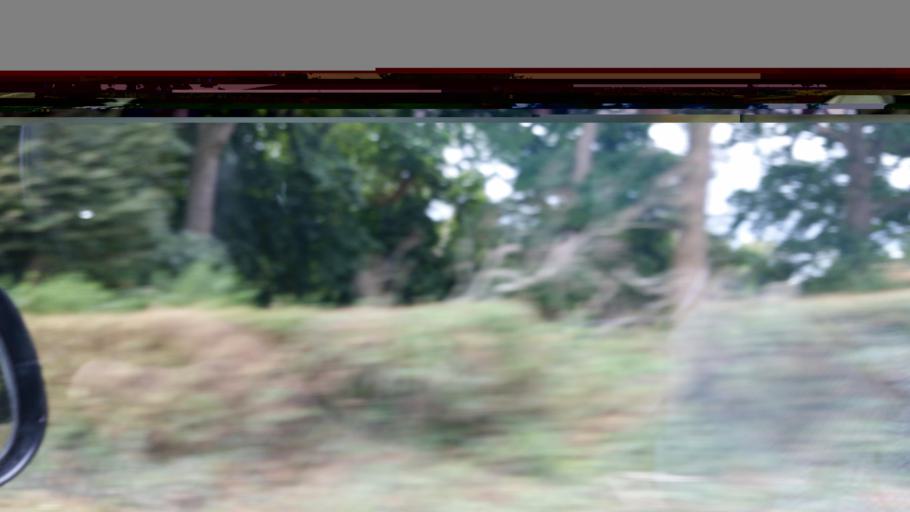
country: IE
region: Leinster
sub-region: Loch Garman
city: Castlebridge
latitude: 52.4097
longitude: -6.4082
